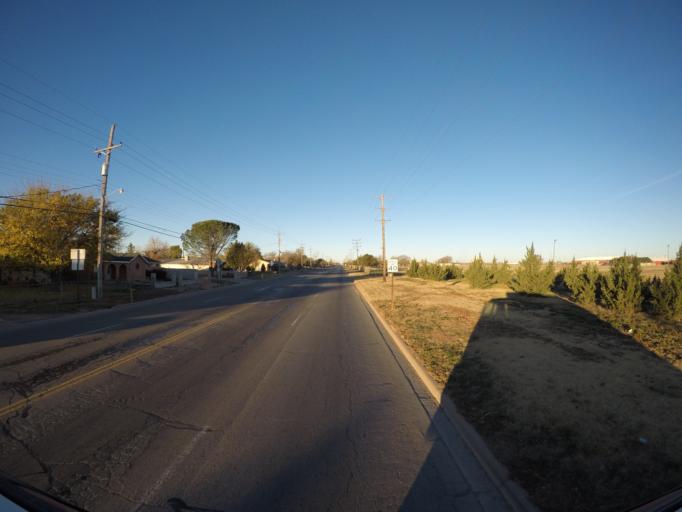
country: US
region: New Mexico
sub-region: Curry County
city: Clovis
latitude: 34.3903
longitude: -103.1799
